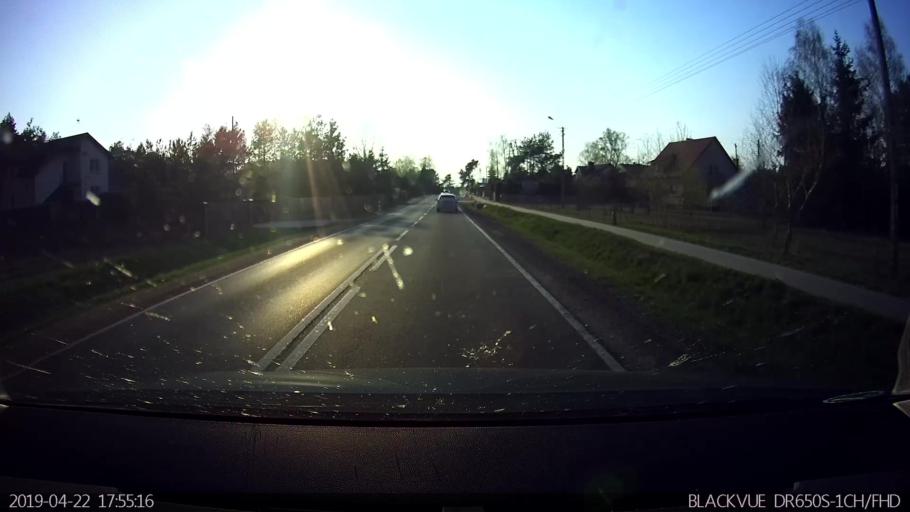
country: PL
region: Masovian Voivodeship
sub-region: Powiat wegrowski
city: Stoczek
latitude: 52.4612
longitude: 21.9206
